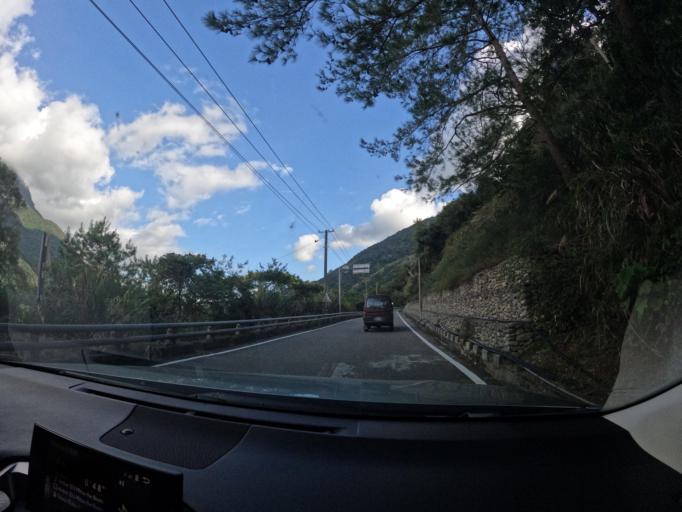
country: TW
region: Taiwan
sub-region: Taitung
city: Taitung
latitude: 23.1629
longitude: 121.0511
